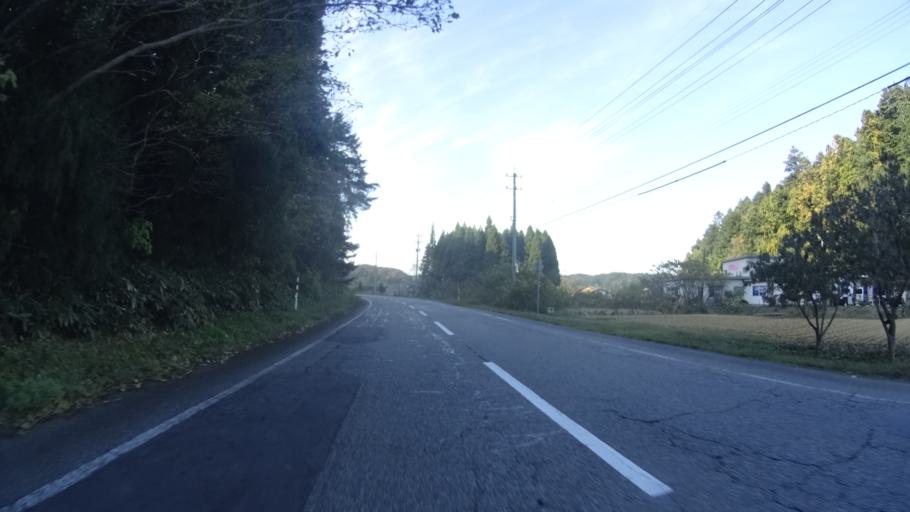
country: JP
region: Ishikawa
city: Hakui
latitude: 37.0155
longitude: 136.7956
